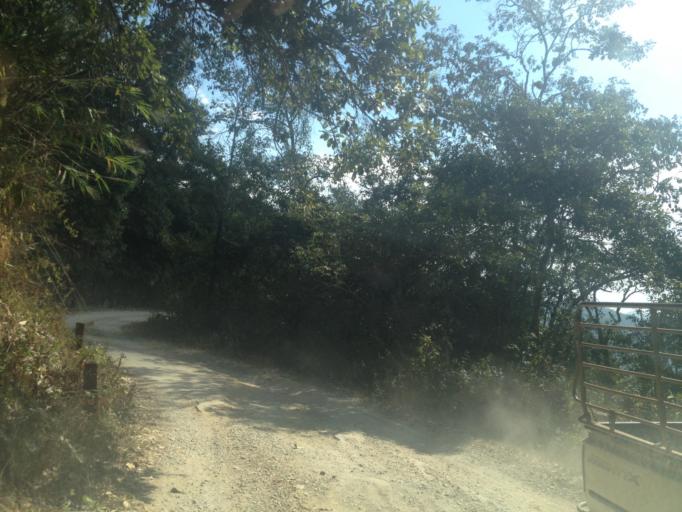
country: TH
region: Mae Hong Son
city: Ban Huai I Huak
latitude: 18.1140
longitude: 98.1574
